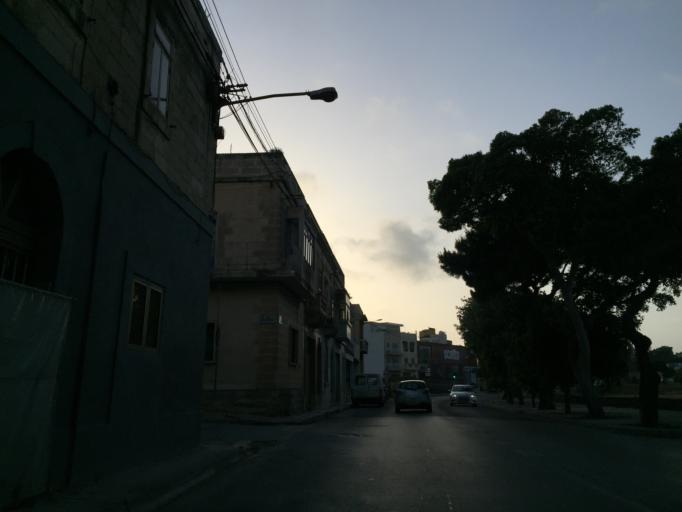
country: MT
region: Saint Paul's Bay
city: San Pawl il-Bahar
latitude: 35.9368
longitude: 14.4126
